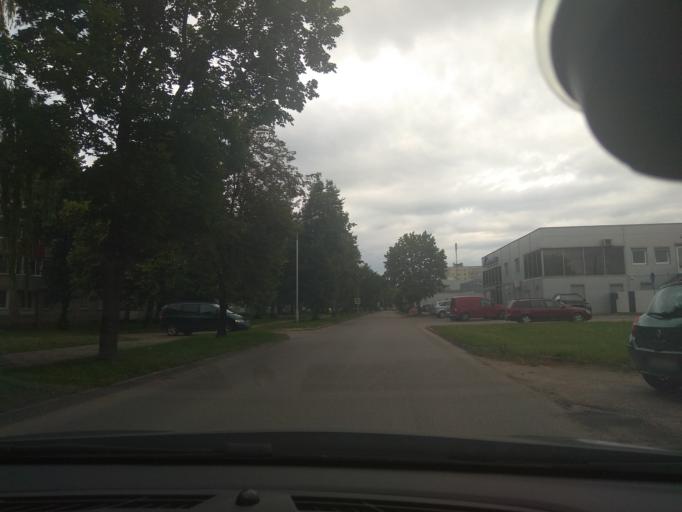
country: LT
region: Marijampoles apskritis
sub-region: Marijampole Municipality
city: Marijampole
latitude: 54.5640
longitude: 23.3622
